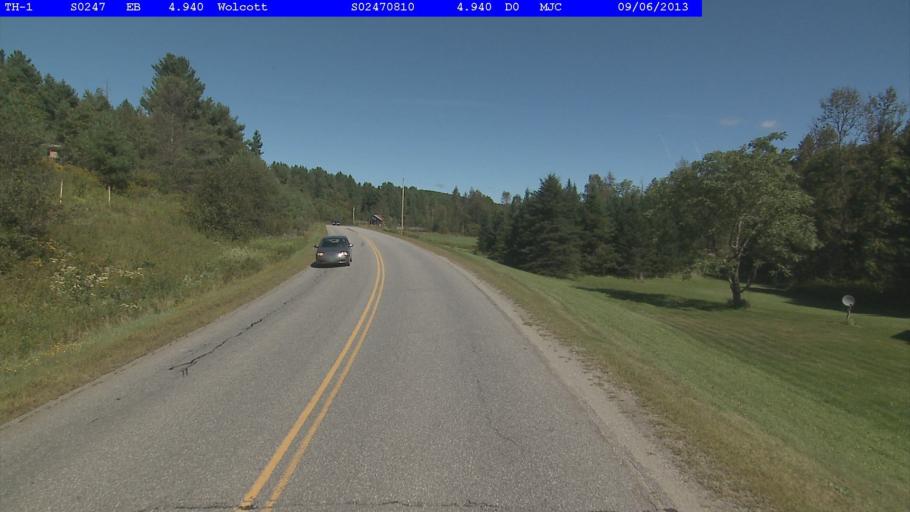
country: US
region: Vermont
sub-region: Caledonia County
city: Hardwick
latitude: 44.6162
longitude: -72.4460
